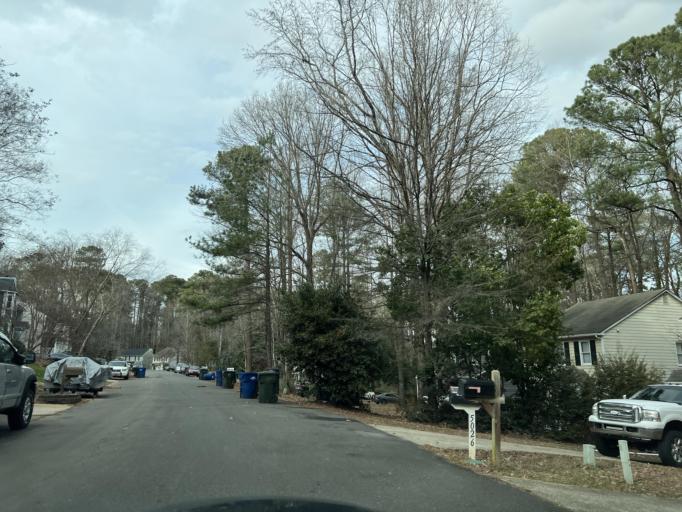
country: US
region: North Carolina
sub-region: Wake County
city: West Raleigh
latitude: 35.7780
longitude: -78.7179
